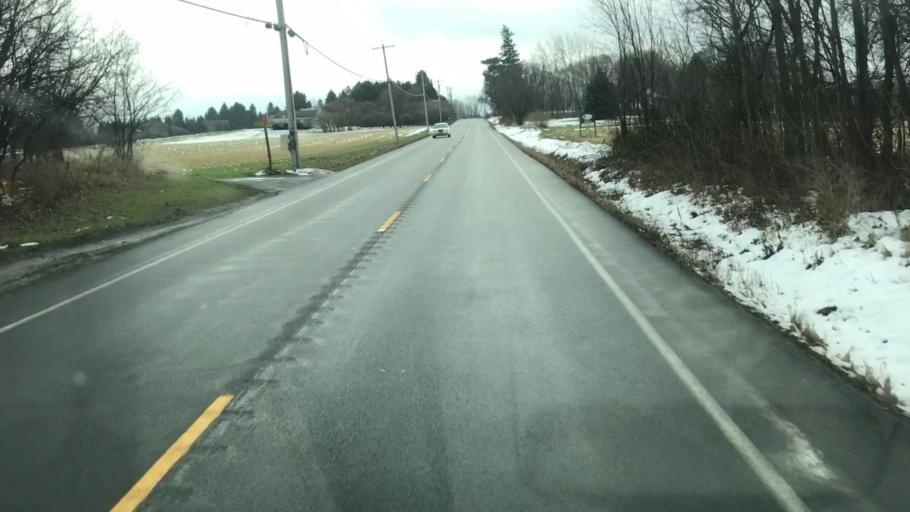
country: US
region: New York
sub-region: Onondaga County
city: Skaneateles
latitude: 42.8431
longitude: -76.3845
